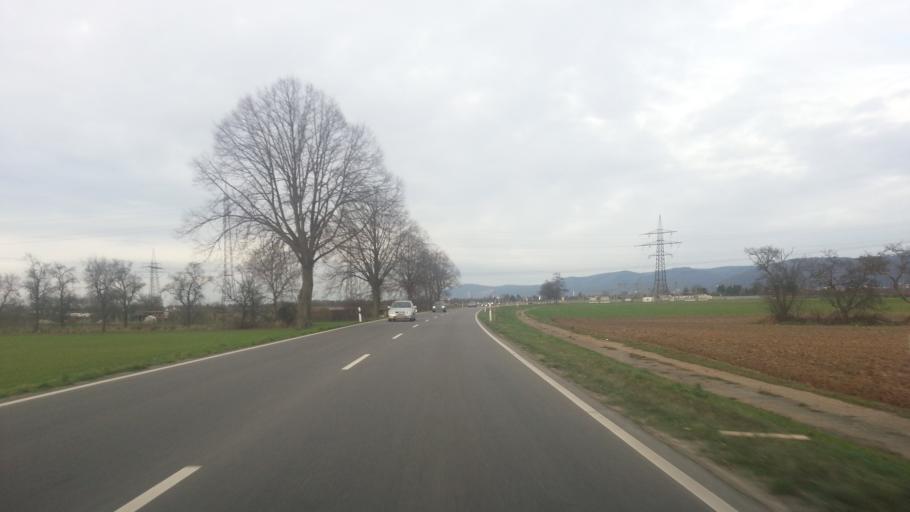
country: DE
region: Baden-Wuerttemberg
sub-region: Karlsruhe Region
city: Sandhausen
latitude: 49.3542
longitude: 8.6606
